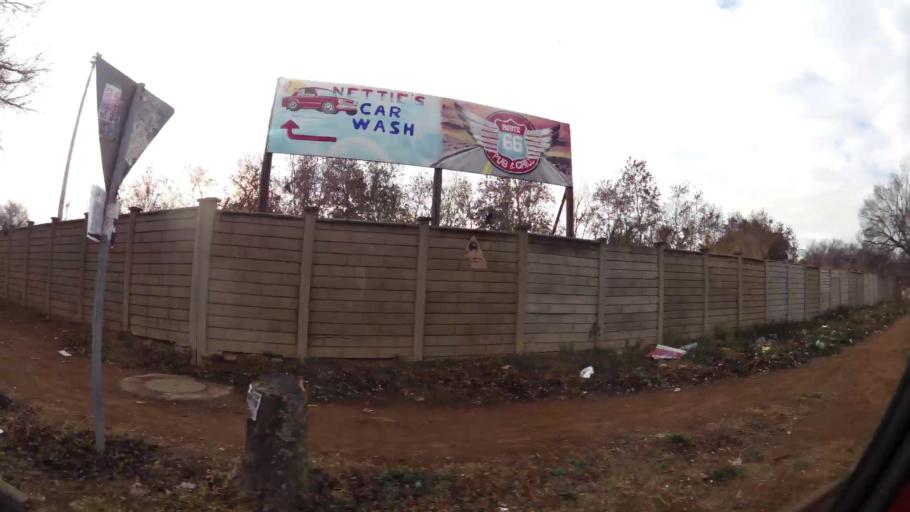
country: ZA
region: Gauteng
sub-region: Sedibeng District Municipality
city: Vanderbijlpark
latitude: -26.6915
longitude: 27.8133
